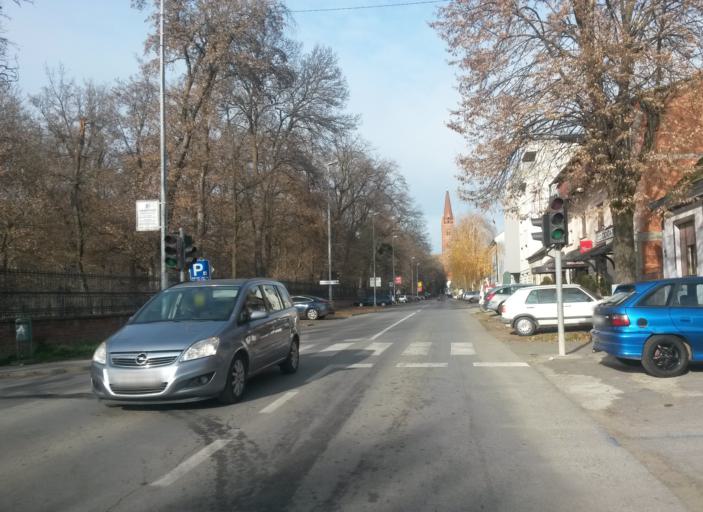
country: HR
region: Osjecko-Baranjska
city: Piskorevci
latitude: 45.3036
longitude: 18.4122
